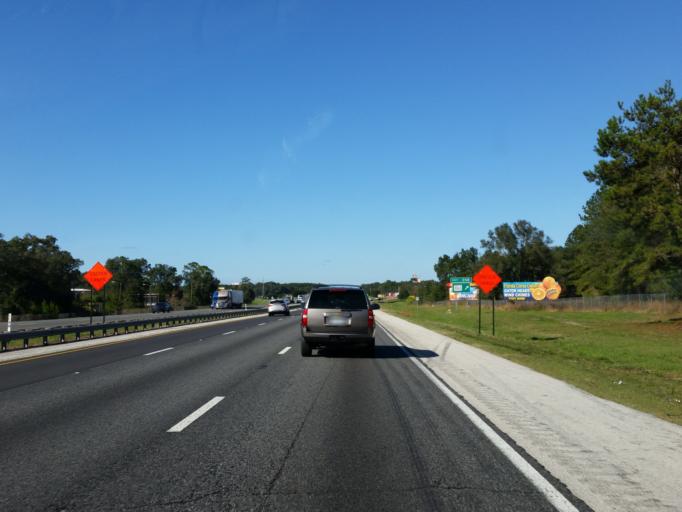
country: US
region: Florida
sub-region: Marion County
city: Ocala
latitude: 29.2602
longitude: -82.1905
